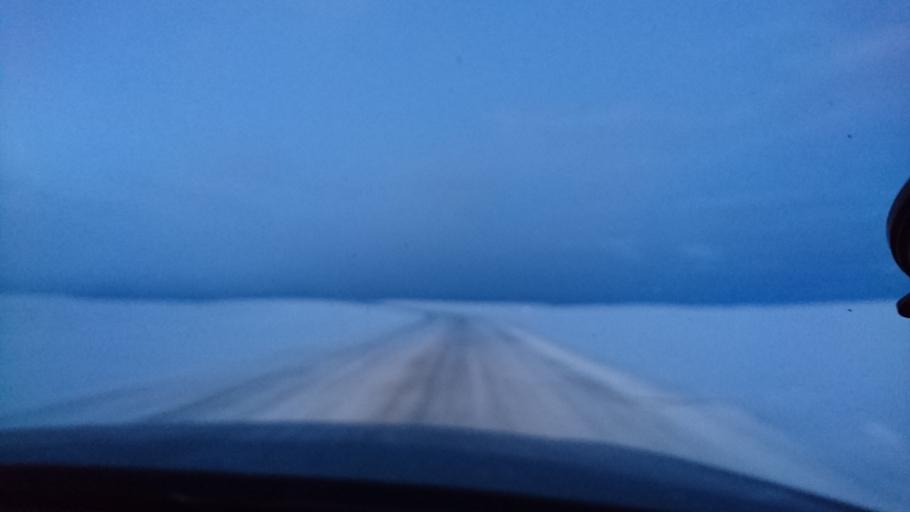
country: NO
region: Finnmark Fylke
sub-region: Nordkapp
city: Honningsvag
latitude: 71.0370
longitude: 25.7979
